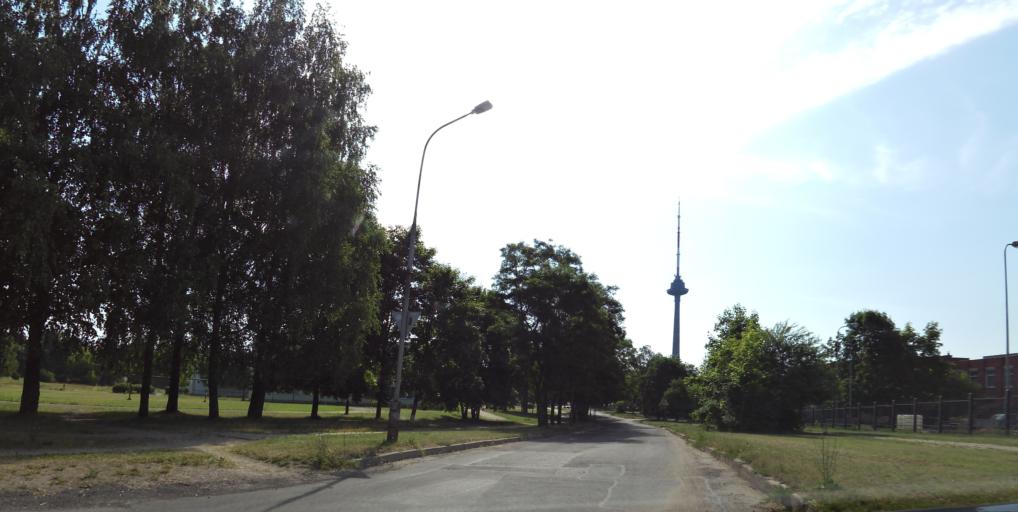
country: LT
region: Vilnius County
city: Pilaite
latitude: 54.6917
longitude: 25.2041
